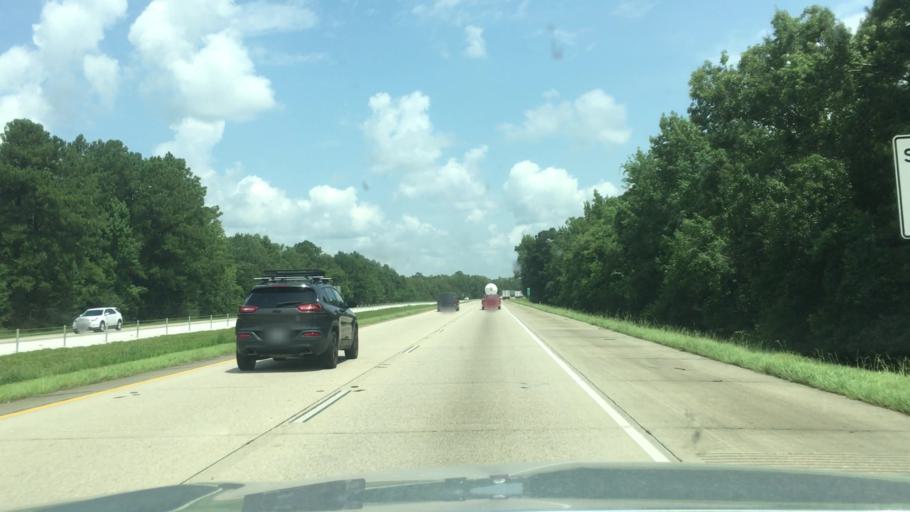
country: US
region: Louisiana
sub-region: Saint Tammany Parish
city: Pearl River
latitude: 30.3621
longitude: -89.7422
